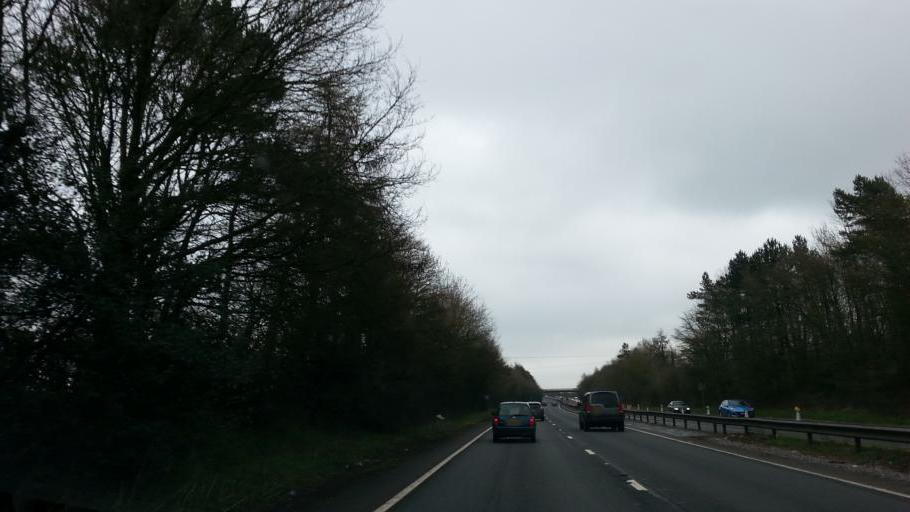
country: GB
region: England
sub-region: Devon
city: Tiverton
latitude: 50.9195
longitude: -3.4187
